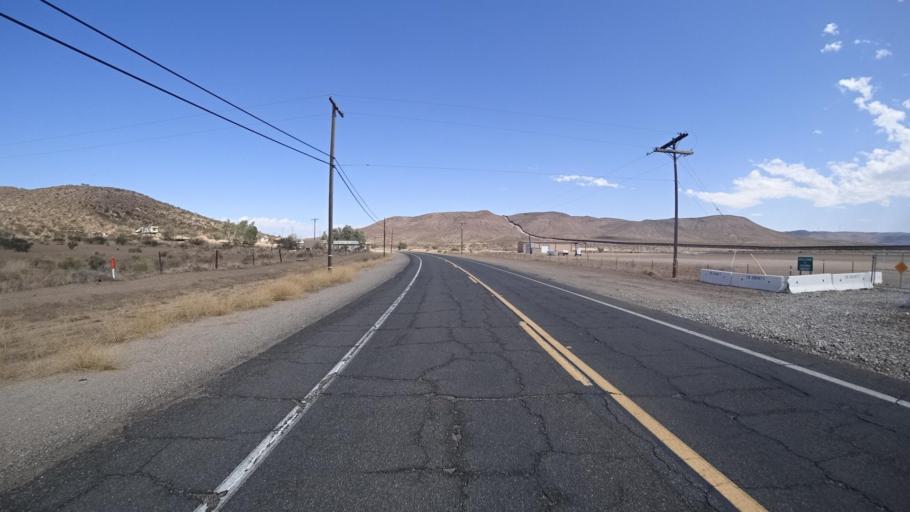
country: MX
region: Baja California
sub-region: Tecate
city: Cereso del Hongo
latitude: 32.6177
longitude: -116.1669
